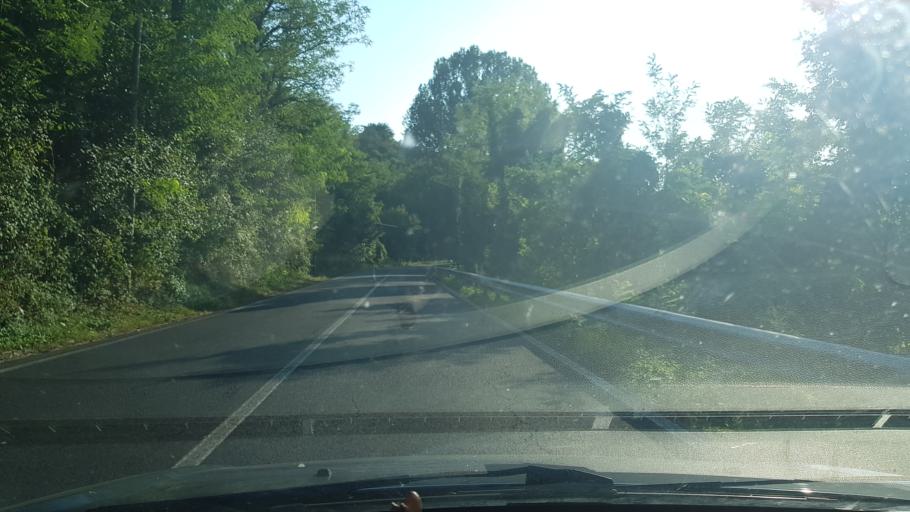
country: IT
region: Friuli Venezia Giulia
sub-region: Provincia di Gorizia
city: Farra d'Isonzo
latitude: 45.8936
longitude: 13.5341
